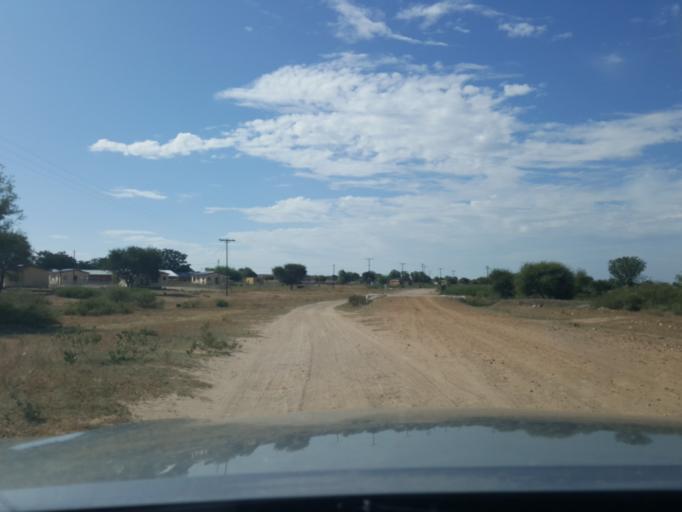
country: BW
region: Kweneng
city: Khudumelapye
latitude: -23.6947
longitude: 24.7172
